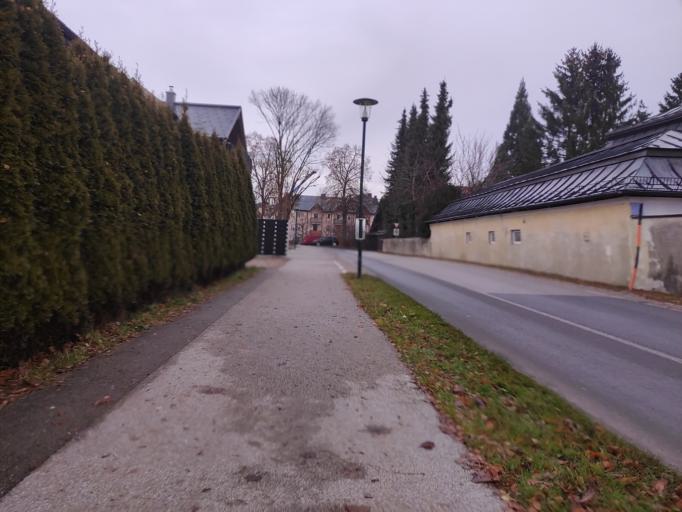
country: AT
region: Salzburg
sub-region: Politischer Bezirk Salzburg-Umgebung
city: Obertrum am See
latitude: 47.9357
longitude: 13.0759
